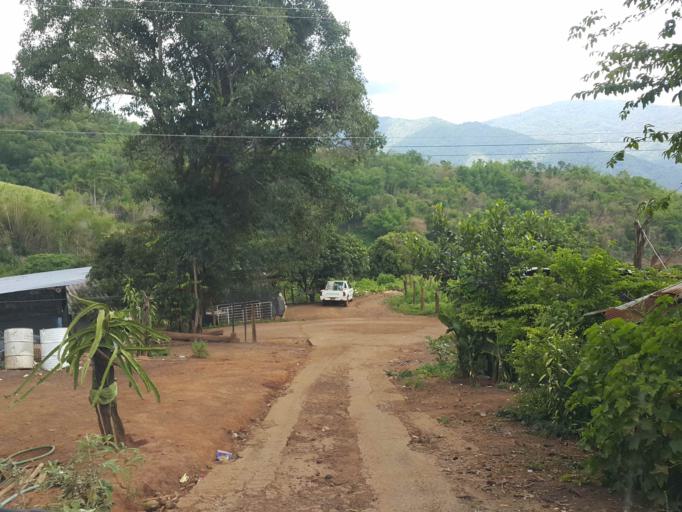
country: TH
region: Chiang Mai
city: Samoeng
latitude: 18.7830
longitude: 98.8248
